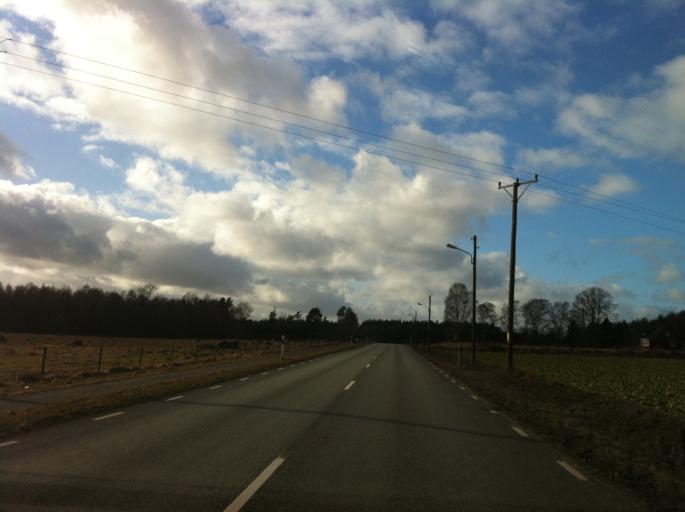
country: SE
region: Skane
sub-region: Bromolla Kommun
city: Bromoella
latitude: 56.0625
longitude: 14.5210
